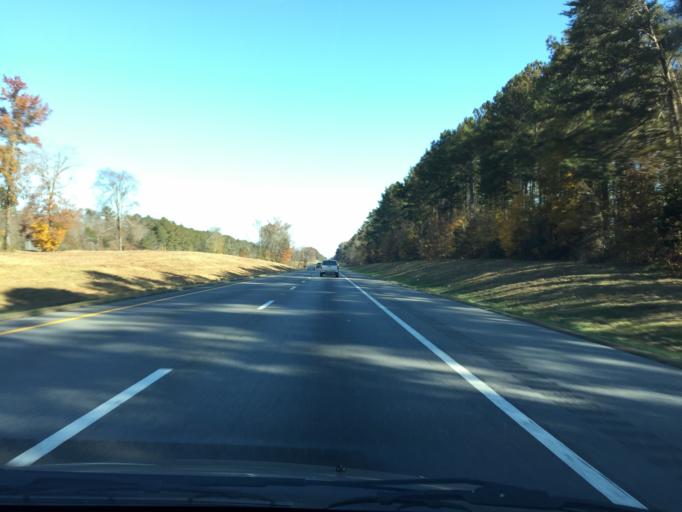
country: US
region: Tennessee
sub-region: Bradley County
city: Hopewell
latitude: 35.2342
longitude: -84.8510
